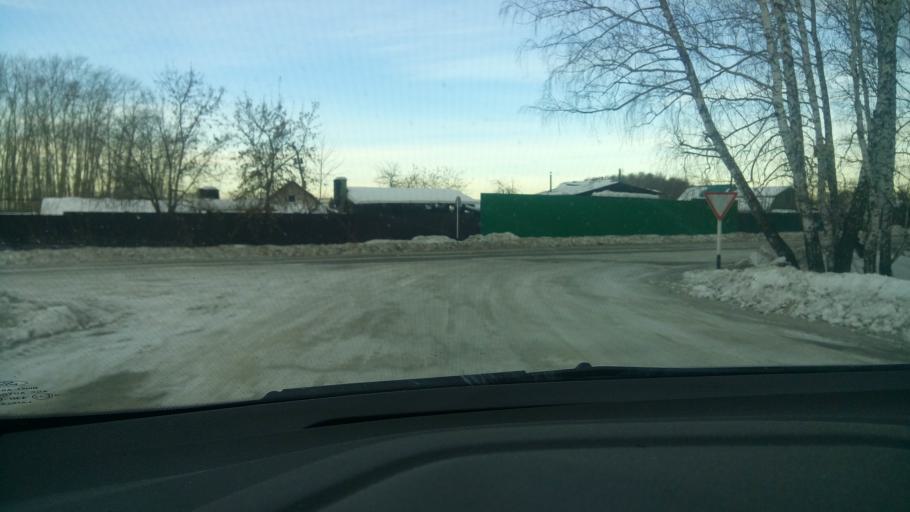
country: RU
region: Chelyabinsk
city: Ozersk
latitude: 55.7749
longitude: 60.7514
